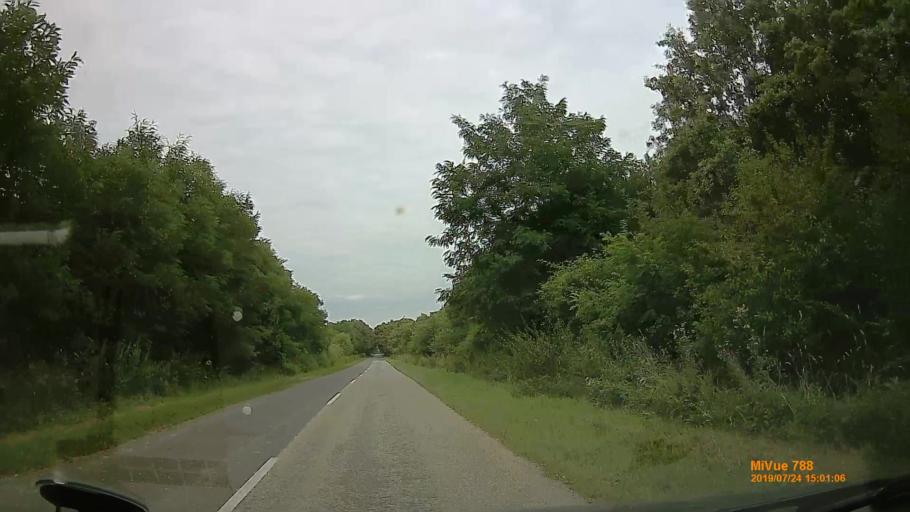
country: HU
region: Szabolcs-Szatmar-Bereg
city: Vasarosnameny
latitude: 48.2299
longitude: 22.3825
